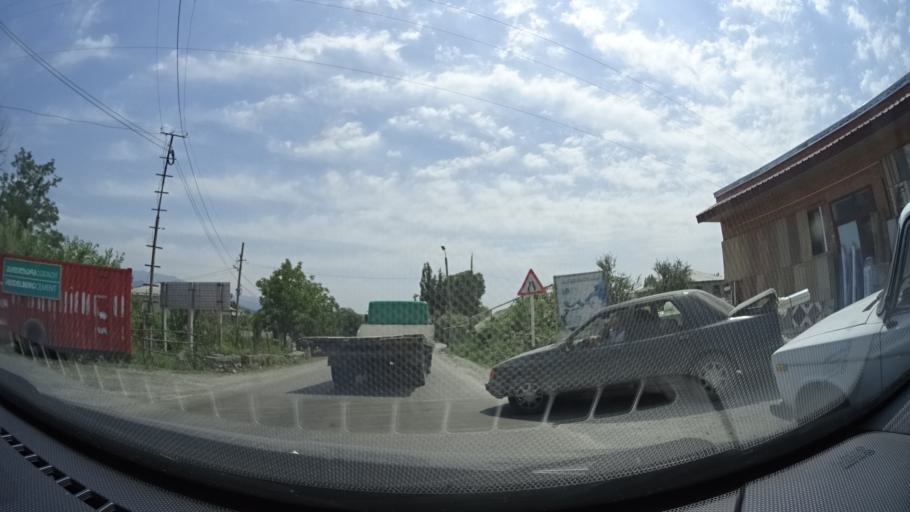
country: GE
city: Bagdadi
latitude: 41.8413
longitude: 46.1388
